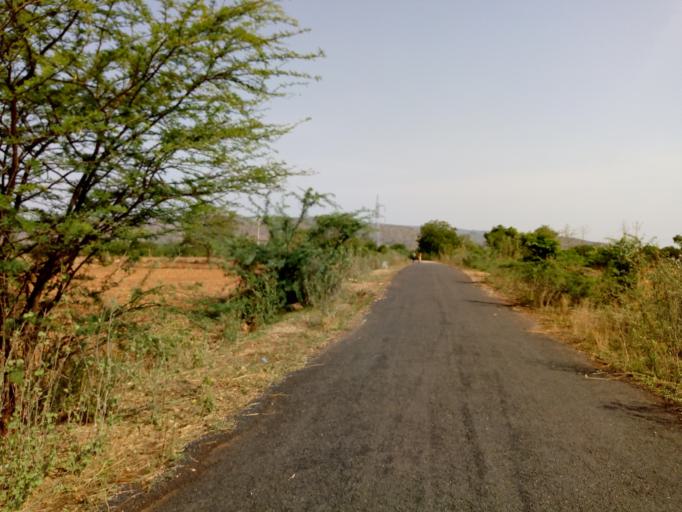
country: IN
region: Andhra Pradesh
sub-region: Prakasam
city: Cumbum
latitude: 15.7124
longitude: 79.0840
